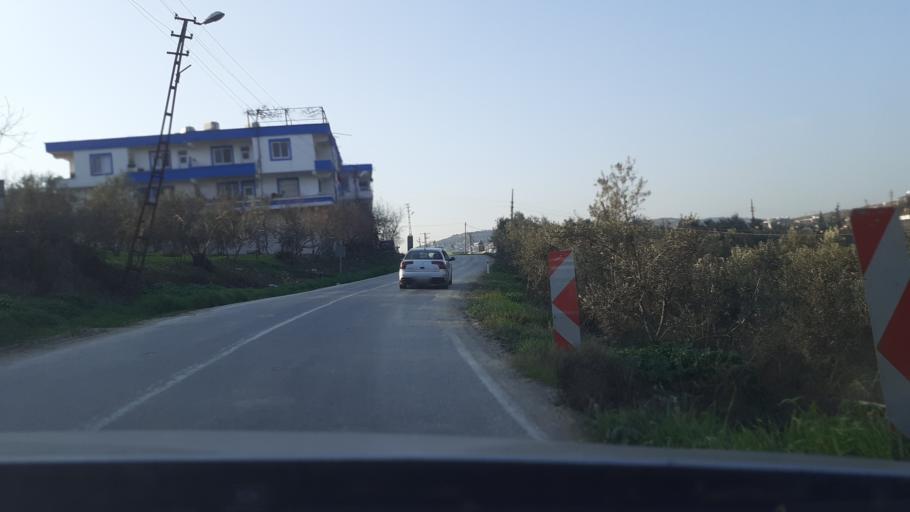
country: TR
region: Hatay
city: Fatikli
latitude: 36.1108
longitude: 36.2657
